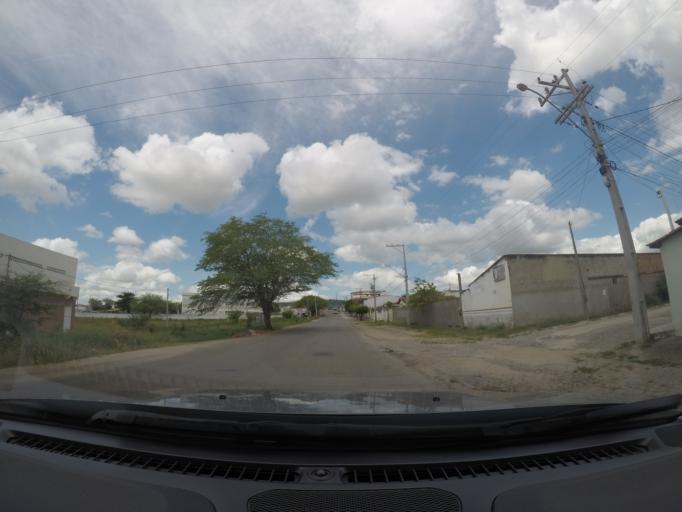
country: BR
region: Bahia
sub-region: Ipira
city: Ipira
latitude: -12.1632
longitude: -39.7469
